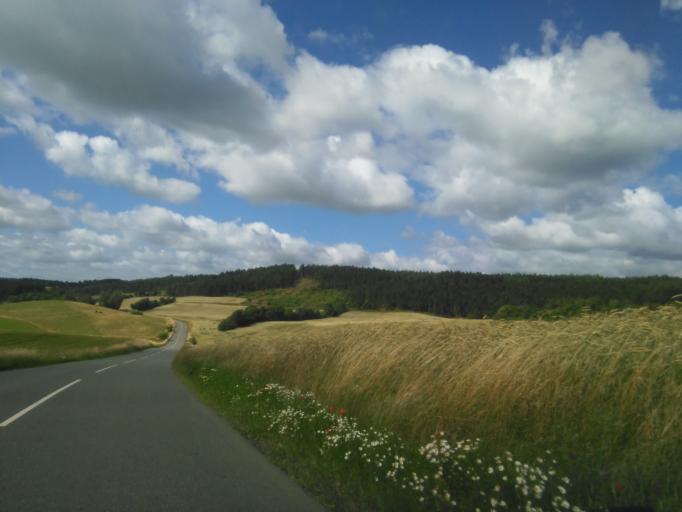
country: DK
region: Central Jutland
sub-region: Syddjurs Kommune
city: Ronde
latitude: 56.1989
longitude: 10.5121
